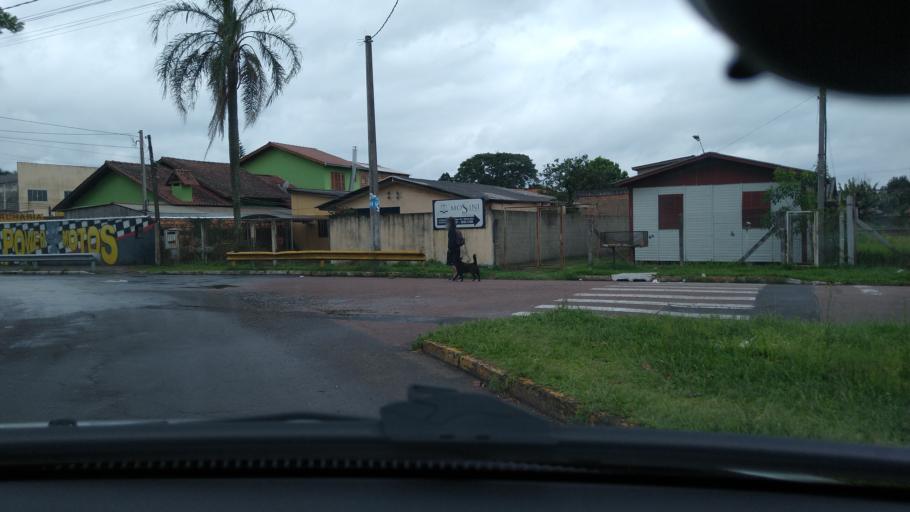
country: BR
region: Rio Grande do Sul
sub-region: Canoas
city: Canoas
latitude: -29.9018
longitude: -51.2168
